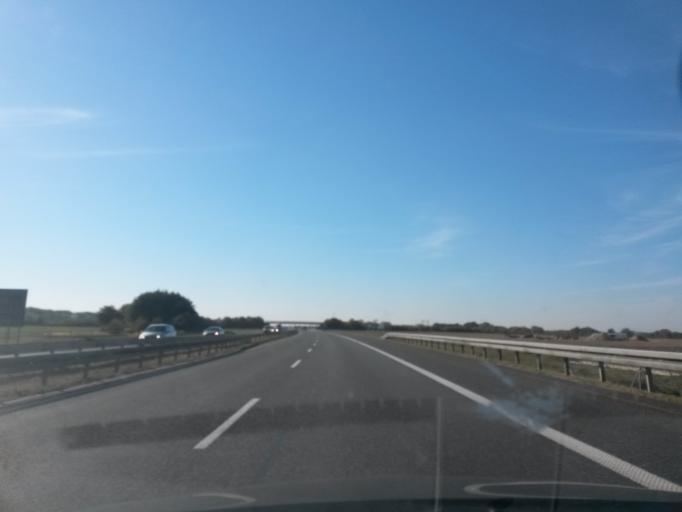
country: PL
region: Opole Voivodeship
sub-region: Powiat brzeski
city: Grodkow
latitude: 50.7691
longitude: 17.3997
